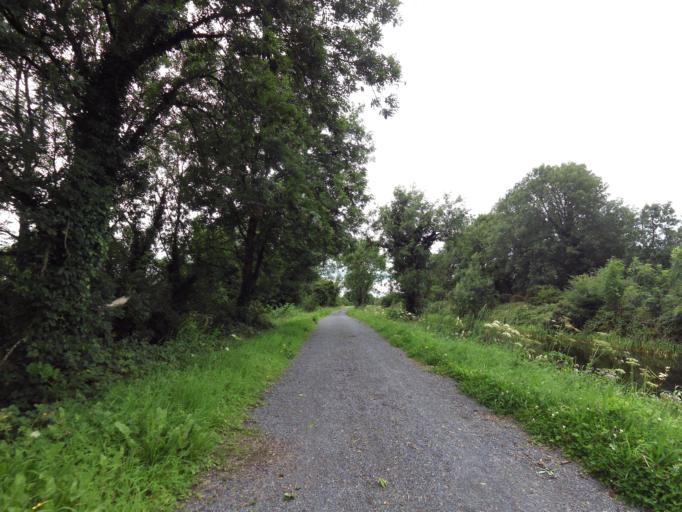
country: IE
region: Leinster
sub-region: An Iarmhi
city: An Muileann gCearr
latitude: 53.5095
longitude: -7.4220
